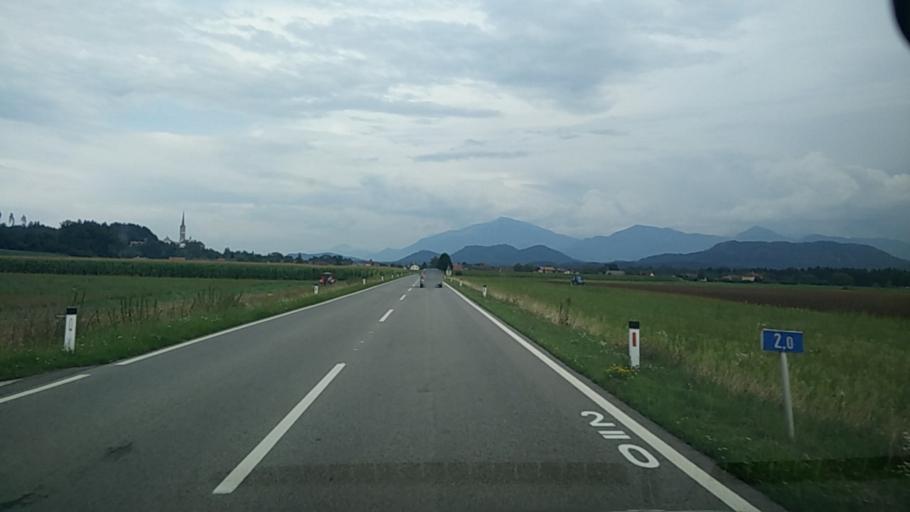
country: AT
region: Carinthia
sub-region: Politischer Bezirk Klagenfurt Land
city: Grafenstein
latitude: 46.6385
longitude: 14.5256
